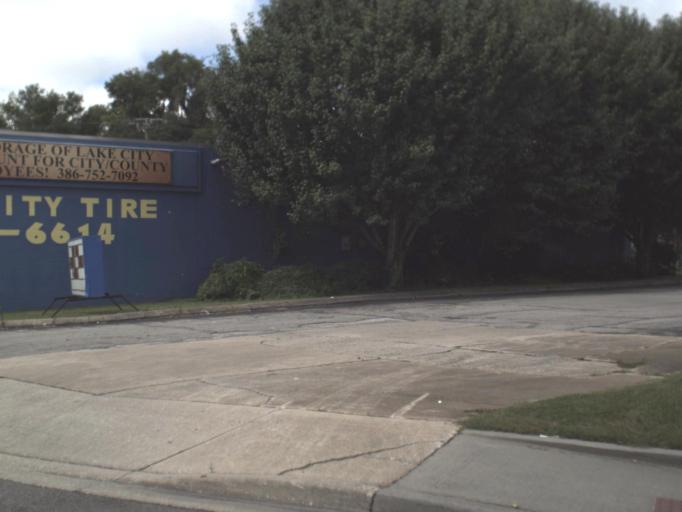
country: US
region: Florida
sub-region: Columbia County
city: Lake City
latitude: 30.1892
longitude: -82.6372
